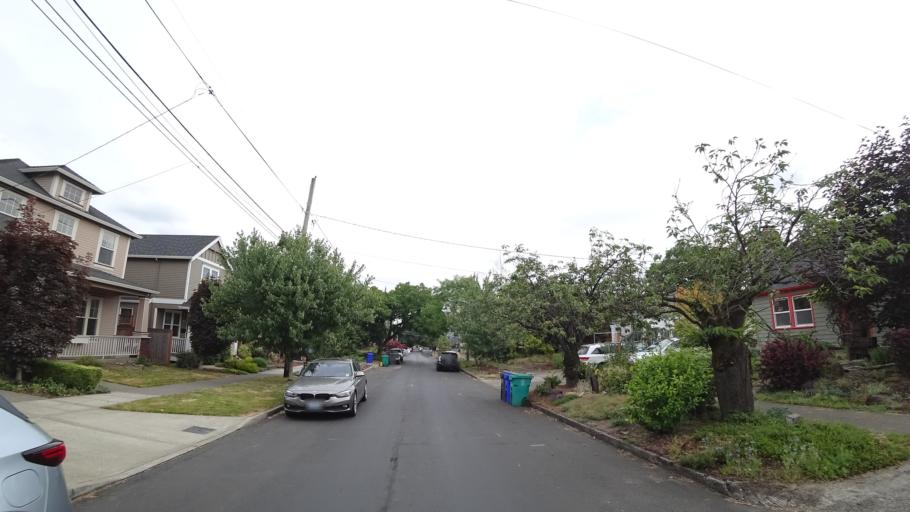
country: US
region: Oregon
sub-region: Multnomah County
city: Portland
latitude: 45.5742
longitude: -122.6832
